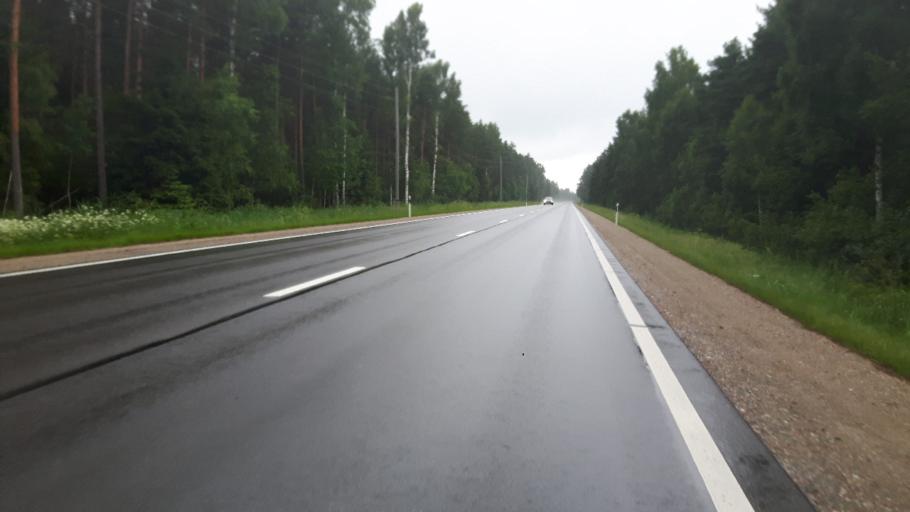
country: LV
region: Rucavas
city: Rucava
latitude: 56.2231
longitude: 21.1210
